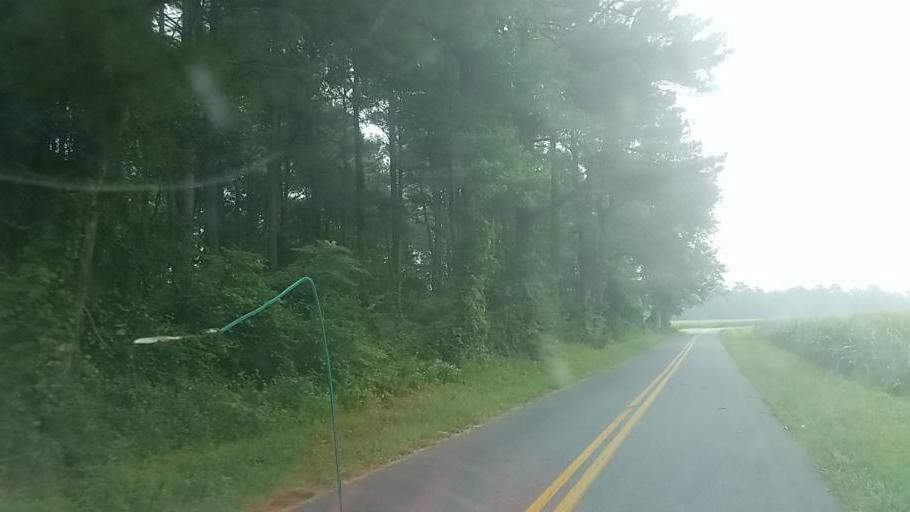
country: US
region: Maryland
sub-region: Wicomico County
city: Pittsville
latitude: 38.4394
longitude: -75.3304
